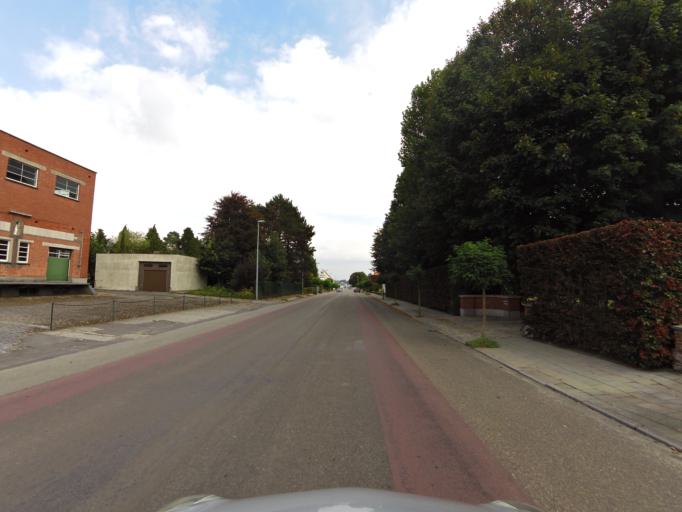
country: BE
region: Flanders
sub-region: Provincie West-Vlaanderen
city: Tielt
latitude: 50.9979
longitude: 3.3422
